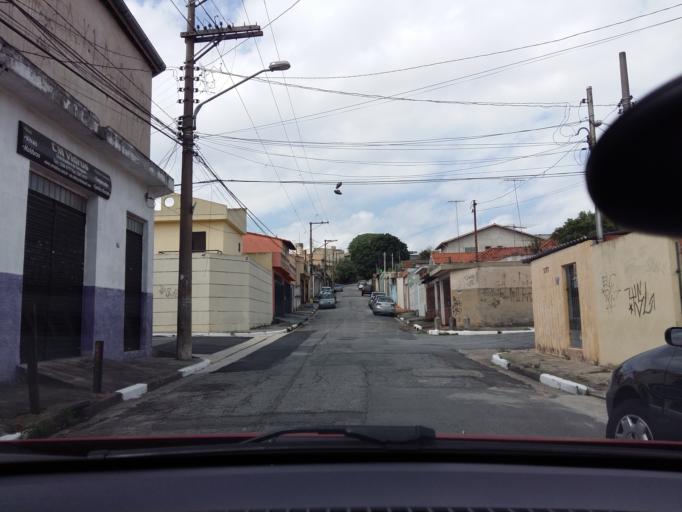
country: BR
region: Sao Paulo
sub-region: Sao Caetano Do Sul
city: Sao Caetano do Sul
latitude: -23.6003
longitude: -46.5636
